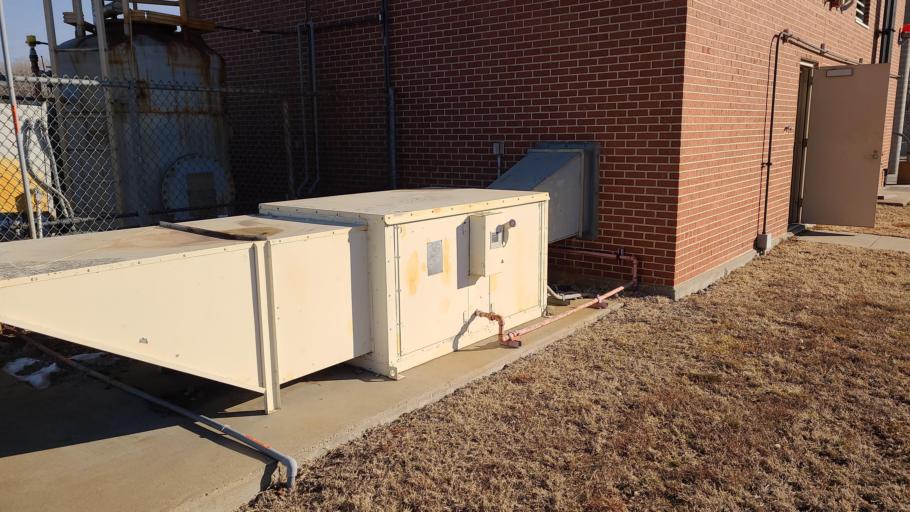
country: US
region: Kansas
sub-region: Douglas County
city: Lawrence
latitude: 38.9320
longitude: -95.2853
